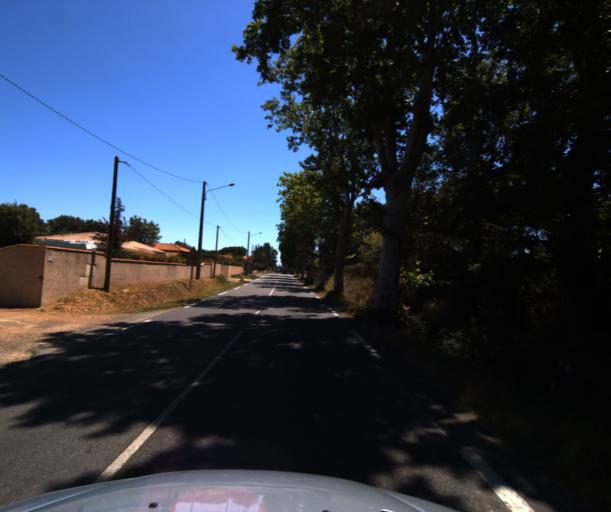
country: FR
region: Midi-Pyrenees
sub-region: Departement de la Haute-Garonne
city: Muret
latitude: 43.4498
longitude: 1.3359
